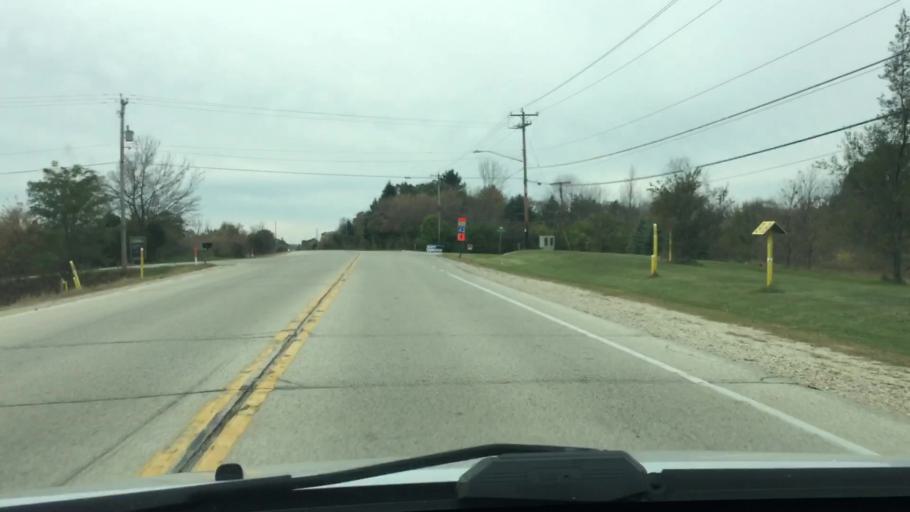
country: US
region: Wisconsin
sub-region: Waukesha County
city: Muskego
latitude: 42.9378
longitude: -88.1716
